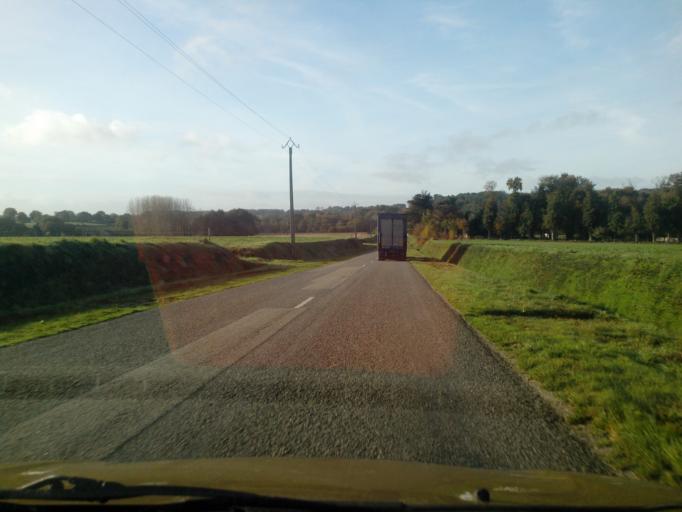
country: FR
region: Brittany
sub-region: Departement du Morbihan
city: Taupont
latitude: 48.0121
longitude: -2.4797
